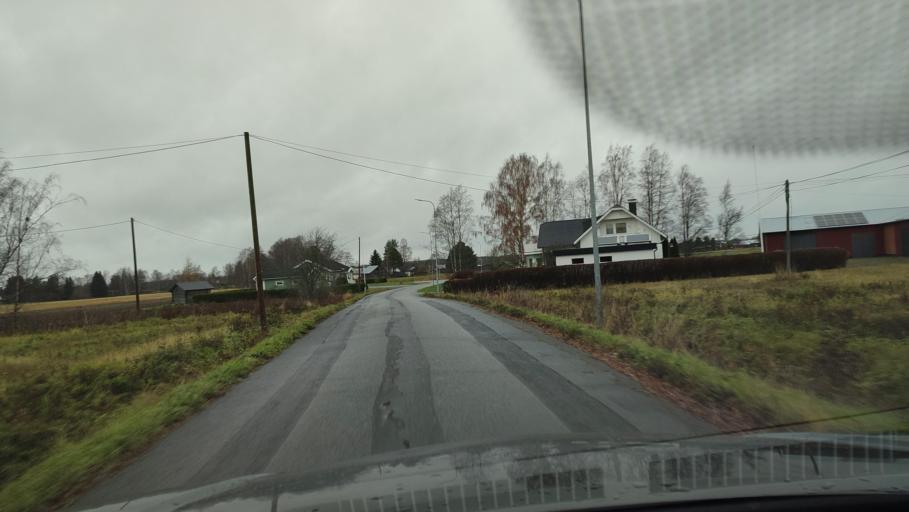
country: FI
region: Ostrobothnia
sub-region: Sydosterbotten
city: Kristinestad
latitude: 62.2506
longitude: 21.5456
